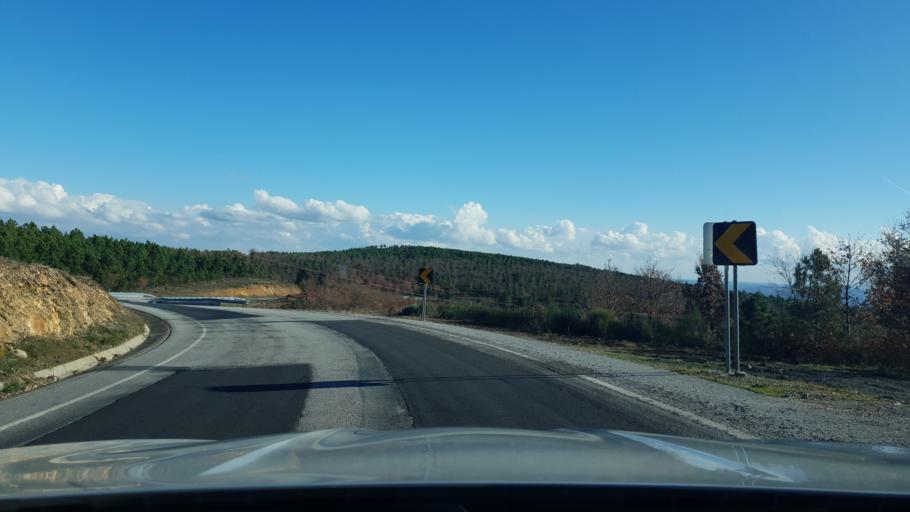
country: PT
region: Braganca
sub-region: Freixo de Espada A Cinta
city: Freixo de Espada a Cinta
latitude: 41.1406
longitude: -6.8086
